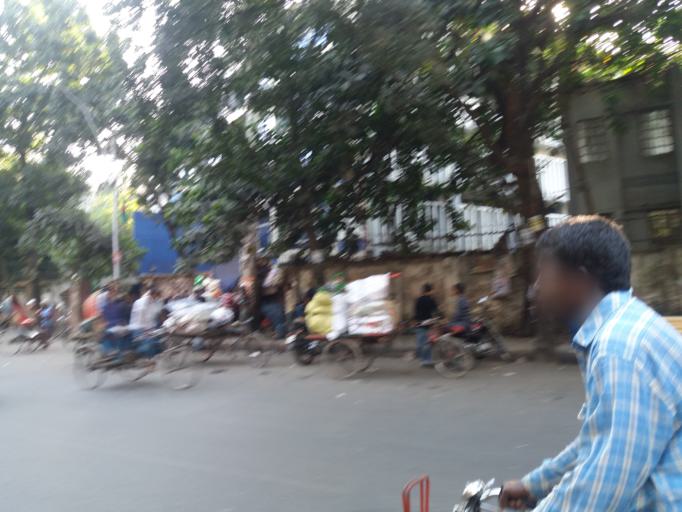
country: BD
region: Dhaka
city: Azimpur
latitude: 23.7291
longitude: 90.3881
